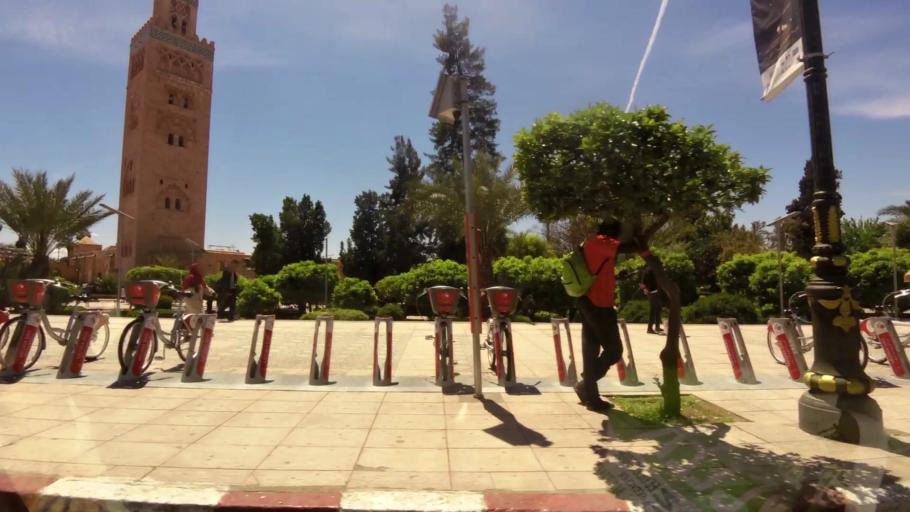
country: MA
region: Marrakech-Tensift-Al Haouz
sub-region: Marrakech
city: Marrakesh
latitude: 31.6251
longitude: -7.9934
